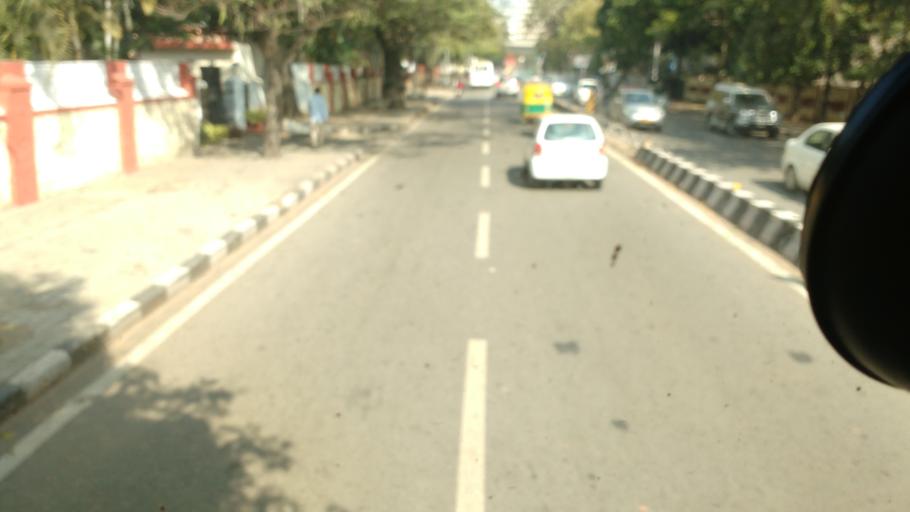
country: IN
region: Karnataka
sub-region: Bangalore Urban
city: Bangalore
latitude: 12.9697
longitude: 77.6197
